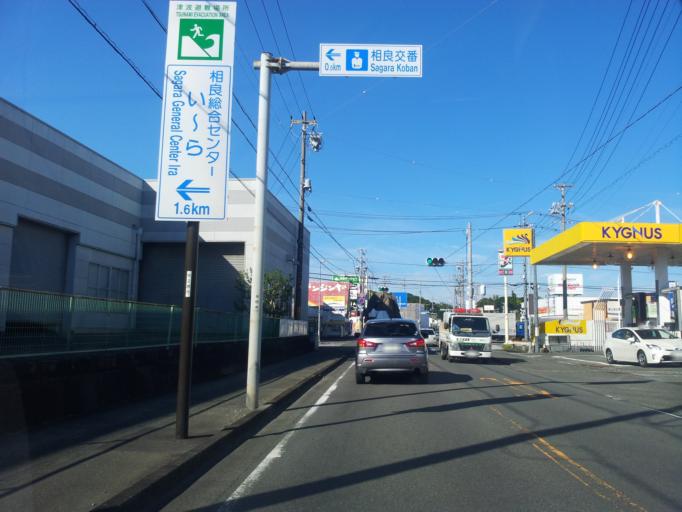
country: JP
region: Shizuoka
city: Sagara
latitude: 34.6859
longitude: 138.1925
